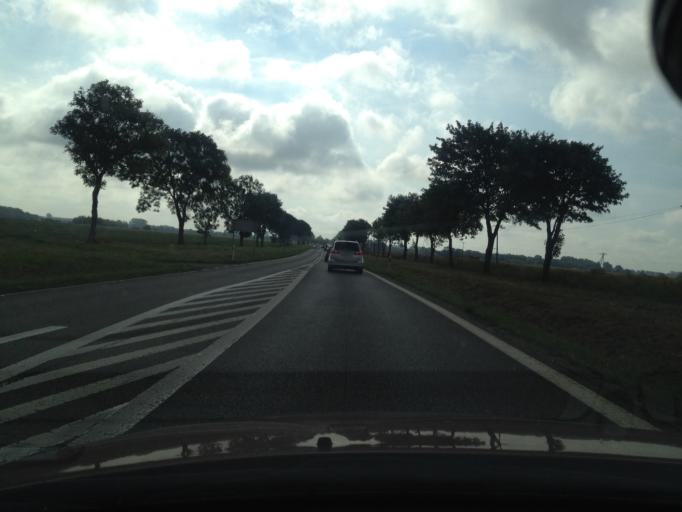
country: PL
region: West Pomeranian Voivodeship
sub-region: Powiat kamienski
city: Kamien Pomorski
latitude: 53.9550
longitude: 14.7930
